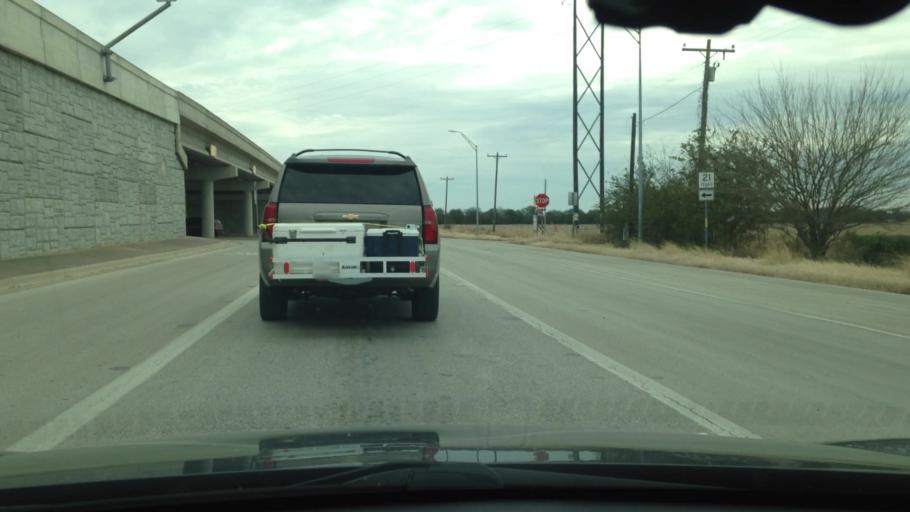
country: US
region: Texas
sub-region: Hays County
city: San Marcos
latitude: 29.8773
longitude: -97.9067
